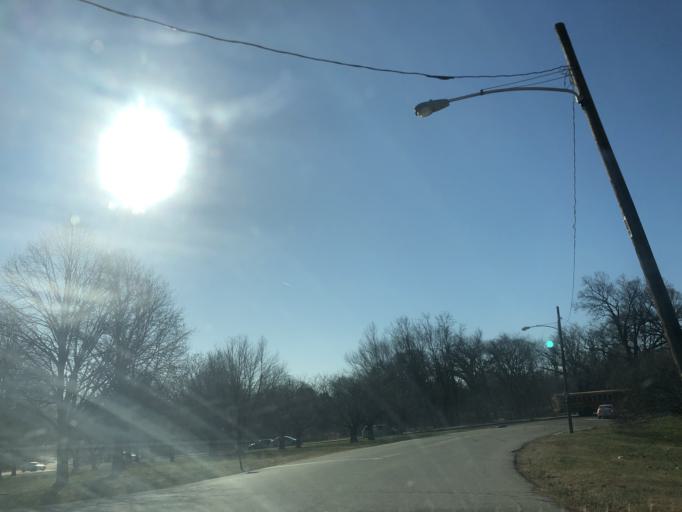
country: US
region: Pennsylvania
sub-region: Montgomery County
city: Bala-Cynwyd
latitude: 39.9867
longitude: -75.2136
